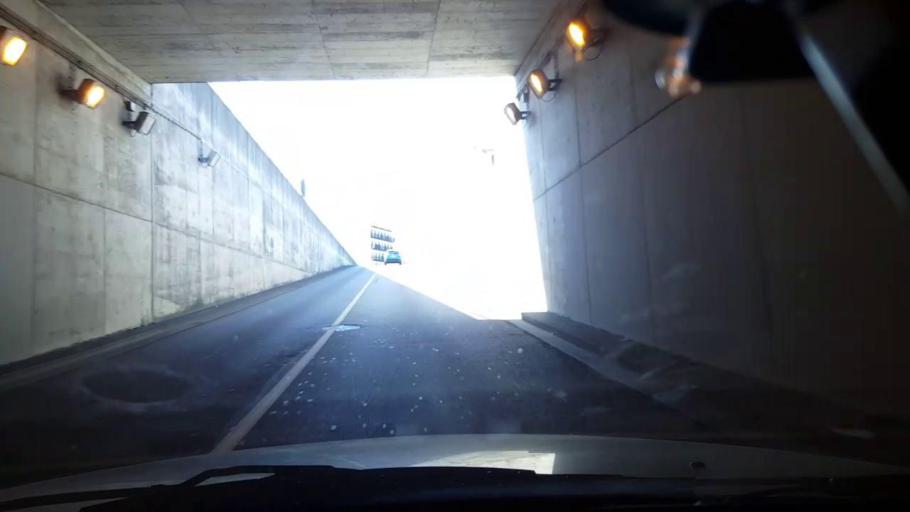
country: PT
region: Porto
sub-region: Vila do Conde
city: Vila do Conde
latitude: 41.3686
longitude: -8.7492
